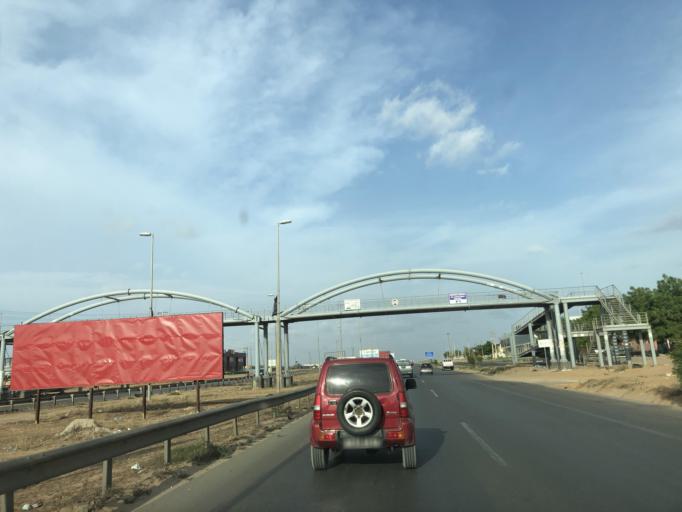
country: AO
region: Luanda
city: Luanda
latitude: -8.9784
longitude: 13.1952
